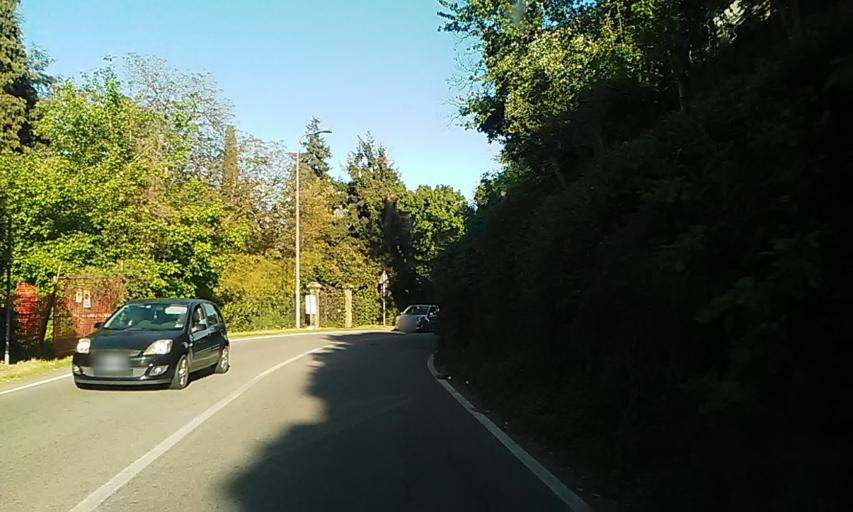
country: IT
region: Piedmont
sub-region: Provincia di Novara
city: Oleggio
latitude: 45.5949
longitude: 8.6361
